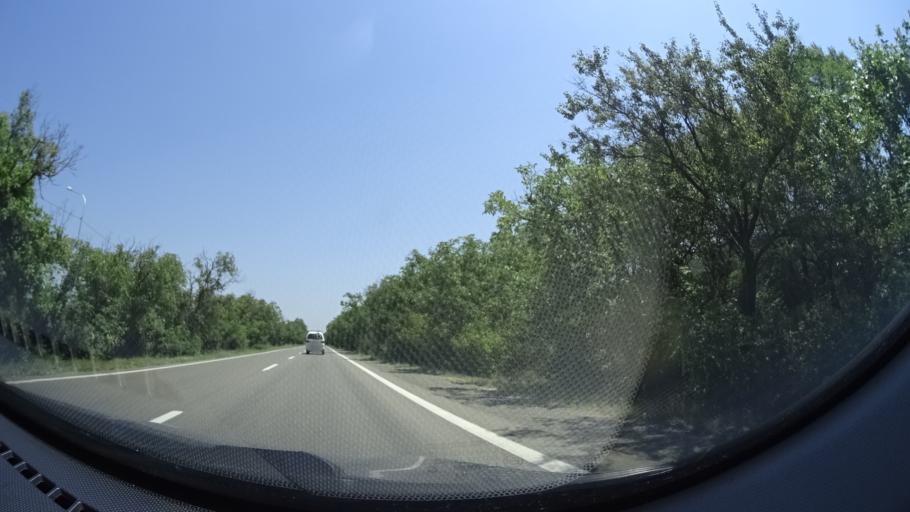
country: GE
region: Shida Kartli
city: Kaspi
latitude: 41.9610
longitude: 44.4797
